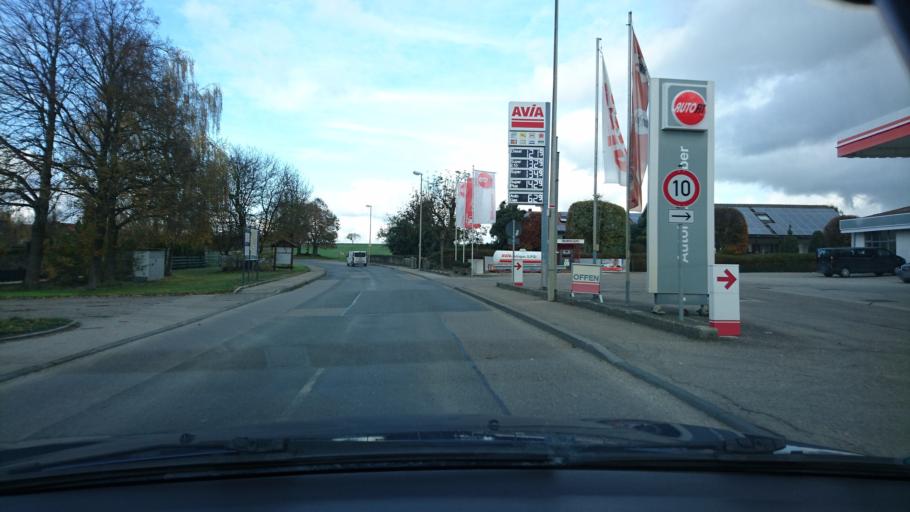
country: DE
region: Baden-Wuerttemberg
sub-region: Regierungsbezirk Stuttgart
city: Lauchheim
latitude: 48.7957
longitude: 10.2602
